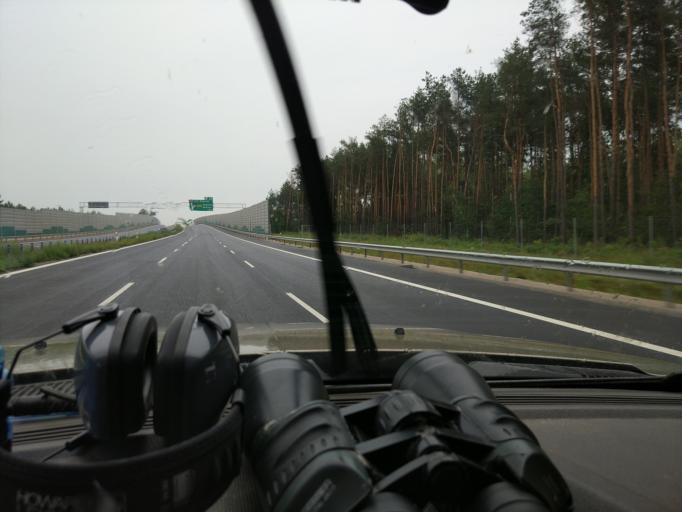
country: PL
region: Masovian Voivodeship
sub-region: Powiat wolominski
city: Radzymin
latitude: 52.3877
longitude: 21.1949
